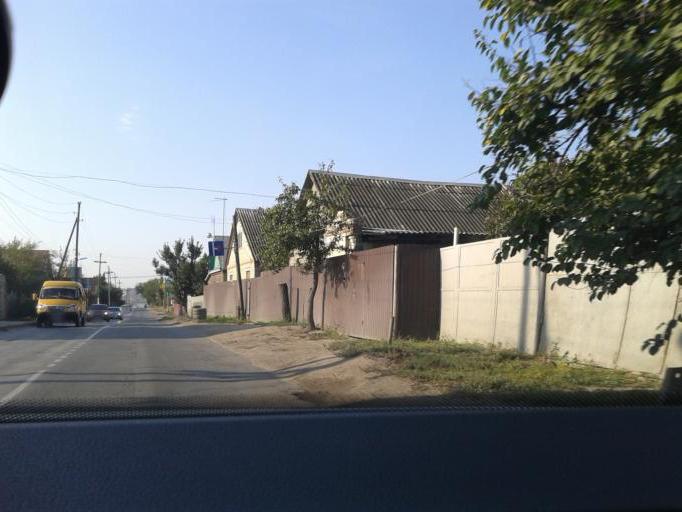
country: RU
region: Volgograd
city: Volgograd
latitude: 48.7008
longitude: 44.4491
